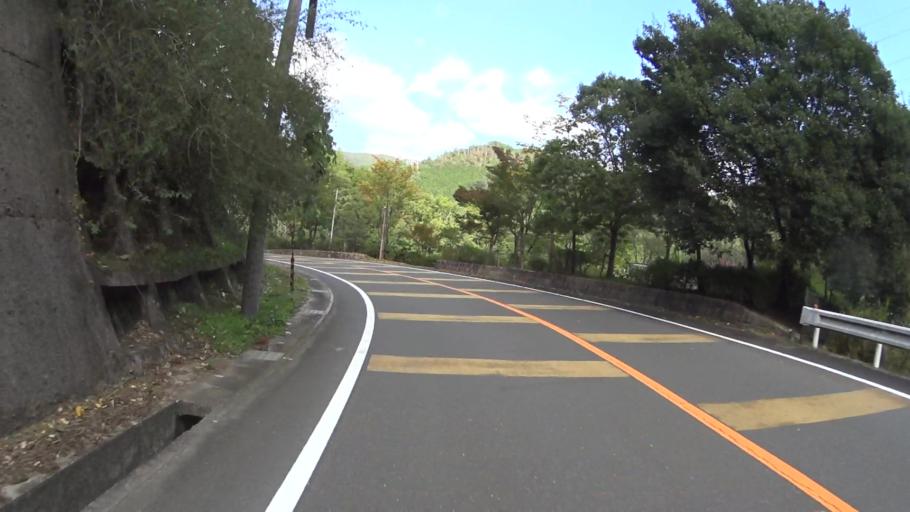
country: JP
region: Kyoto
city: Kameoka
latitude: 35.1291
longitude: 135.5586
